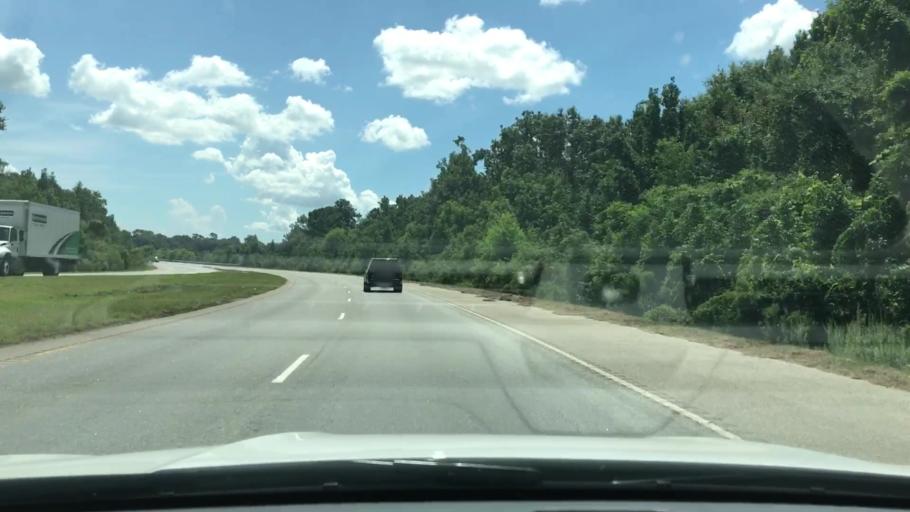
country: US
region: South Carolina
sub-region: Berkeley County
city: Hanahan
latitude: 32.9273
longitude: -79.9962
